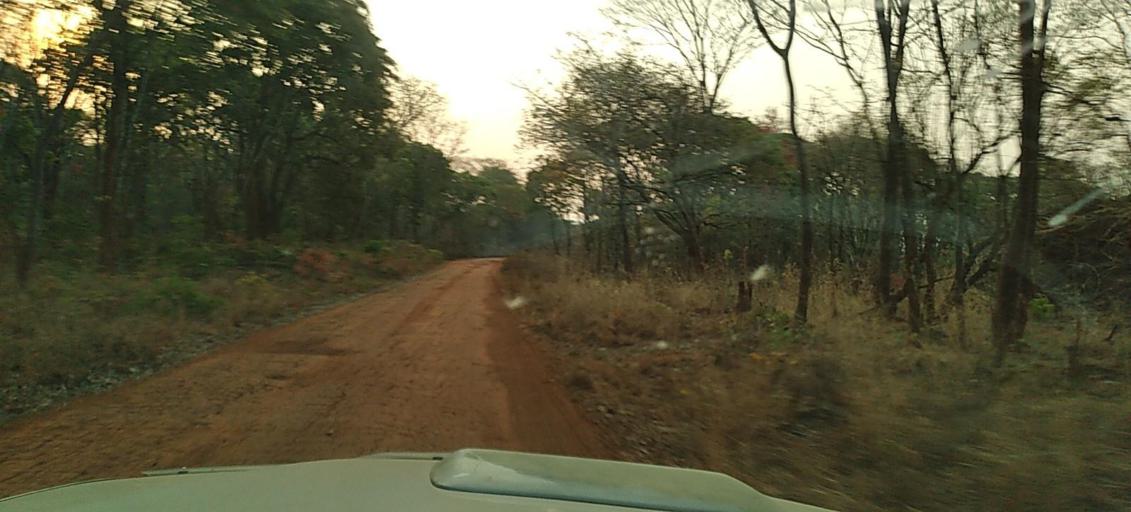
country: ZM
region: North-Western
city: Kasempa
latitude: -13.0767
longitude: 26.3896
